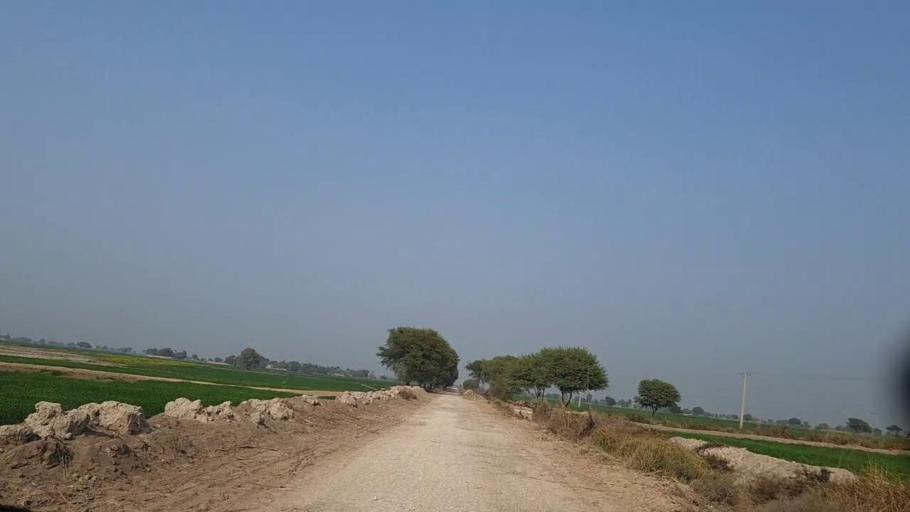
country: PK
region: Sindh
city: Sann
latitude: 26.1912
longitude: 68.1131
